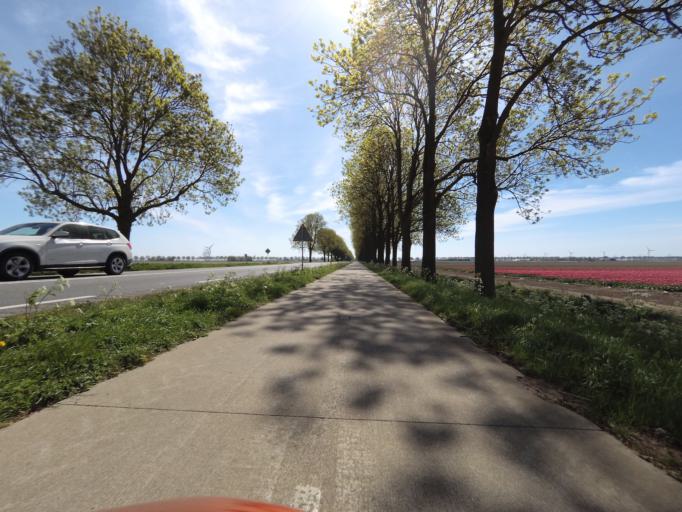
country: NL
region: Flevoland
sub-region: Gemeente Dronten
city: Biddinghuizen
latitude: 52.4909
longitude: 5.6545
